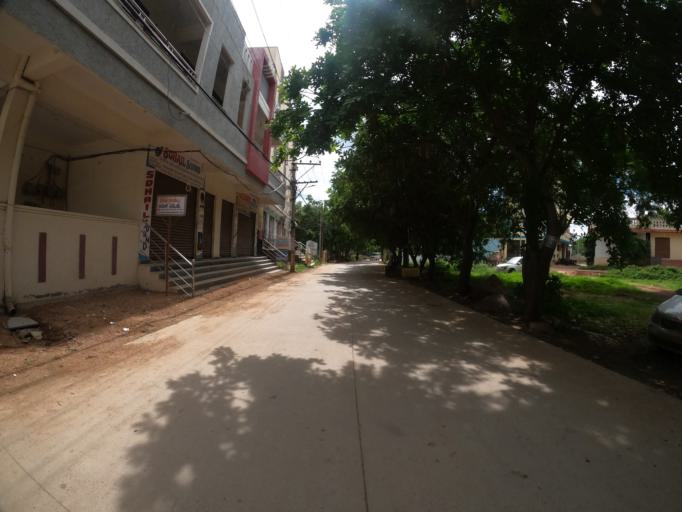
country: IN
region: Telangana
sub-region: Hyderabad
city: Hyderabad
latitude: 17.3518
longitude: 78.3891
